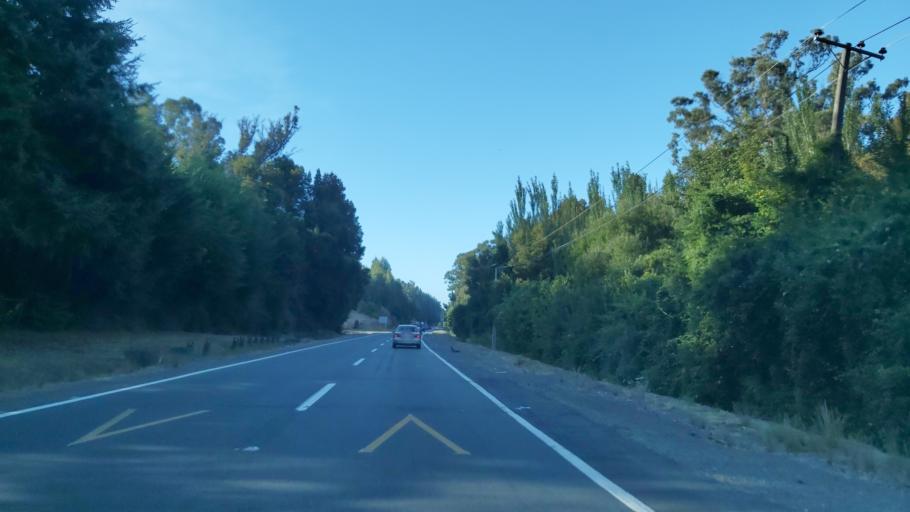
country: CL
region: Biobio
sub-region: Provincia de Concepcion
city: Chiguayante
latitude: -36.8992
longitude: -73.0580
